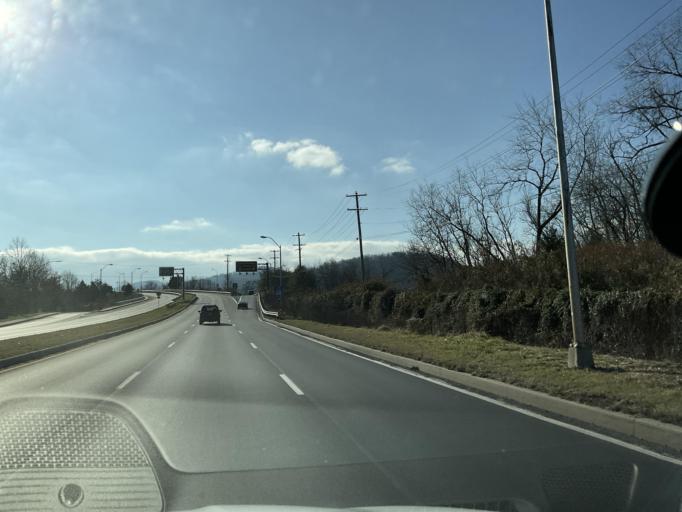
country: US
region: Maryland
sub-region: Allegany County
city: Cumberland
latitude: 39.6472
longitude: -78.7619
